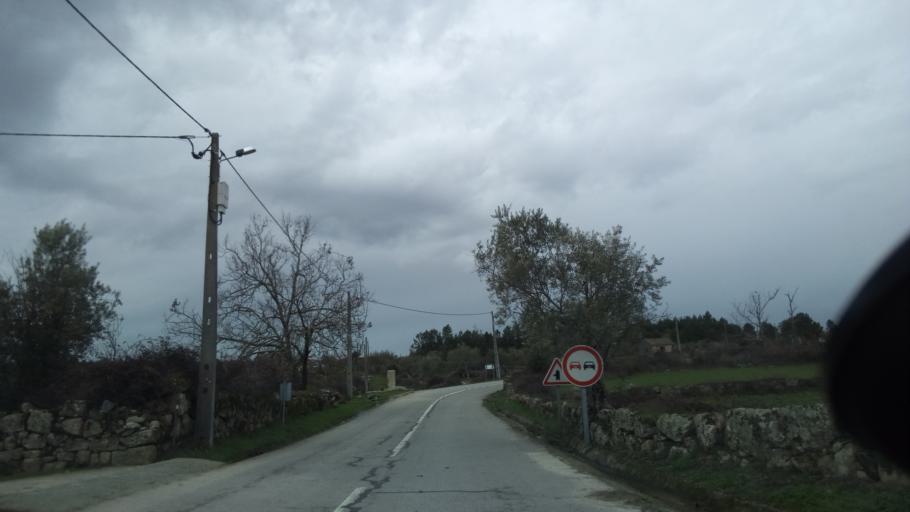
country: PT
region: Guarda
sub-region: Fornos de Algodres
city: Fornos de Algodres
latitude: 40.5901
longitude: -7.4933
